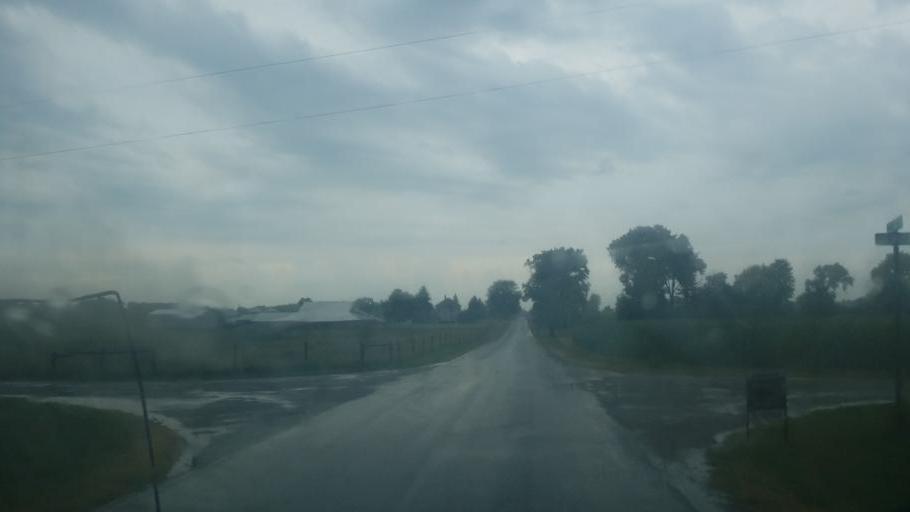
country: US
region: Indiana
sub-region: DeKalb County
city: Butler
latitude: 41.4731
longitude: -84.8524
